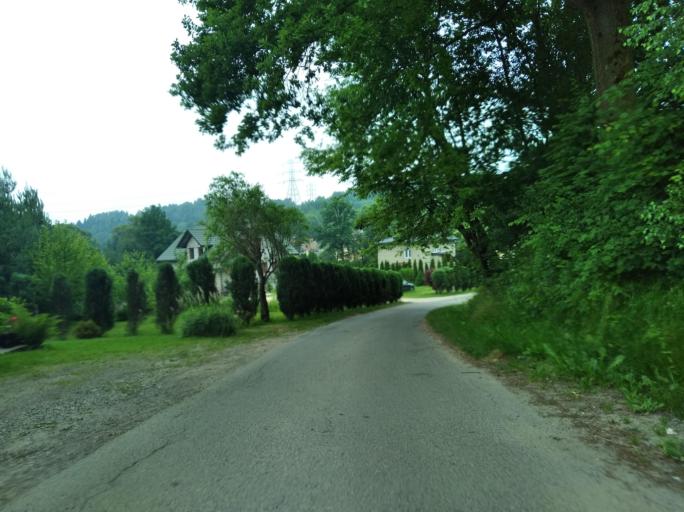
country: PL
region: Subcarpathian Voivodeship
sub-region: Powiat brzozowski
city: Jasienica Rosielna
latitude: 49.7548
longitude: 21.9127
